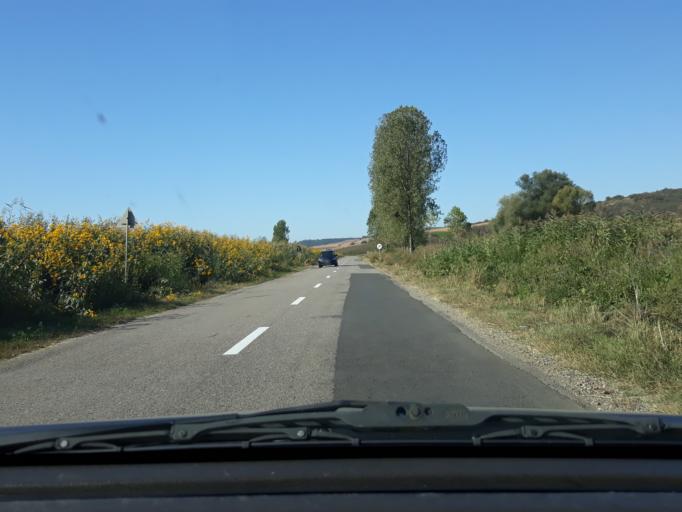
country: RO
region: Salaj
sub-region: Comuna Dobrin
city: Dobrin
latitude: 47.2981
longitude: 23.1241
